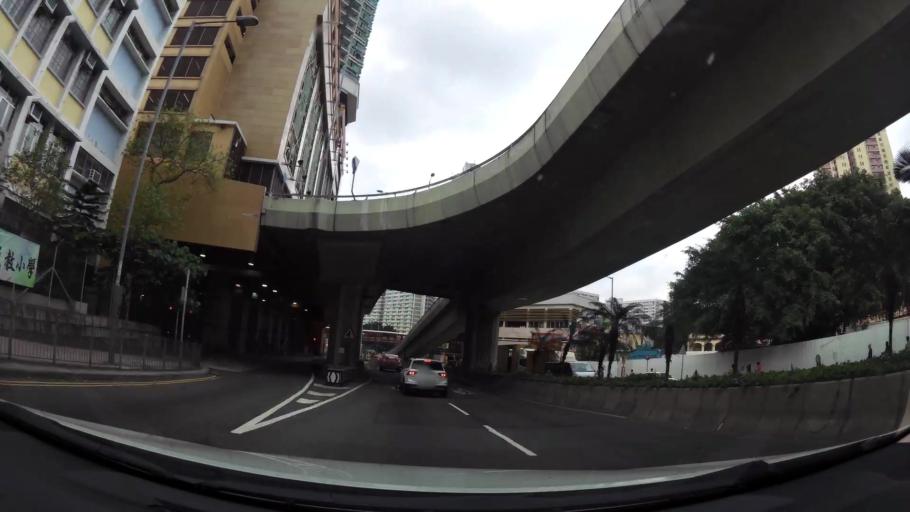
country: HK
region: Wong Tai Sin
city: Wong Tai Sin
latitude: 22.3344
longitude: 114.2105
